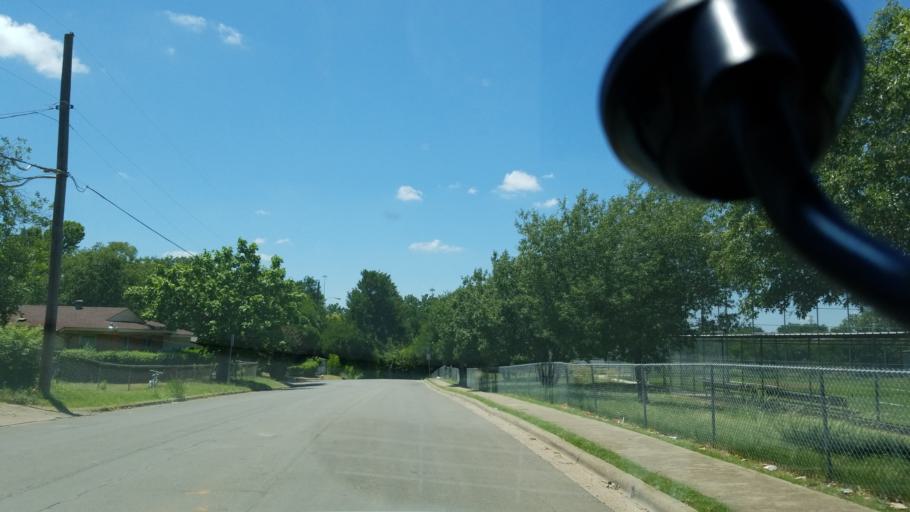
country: US
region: Texas
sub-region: Dallas County
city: Cockrell Hill
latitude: 32.6986
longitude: -96.8172
